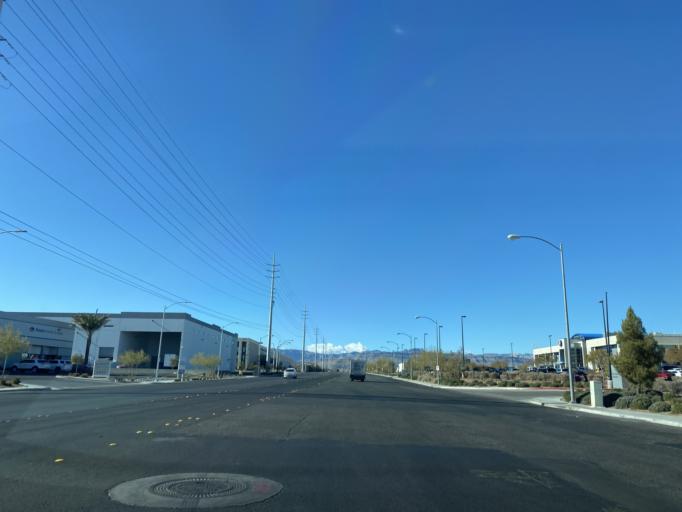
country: US
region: Nevada
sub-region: Clark County
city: Spring Valley
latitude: 36.0709
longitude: -115.2312
